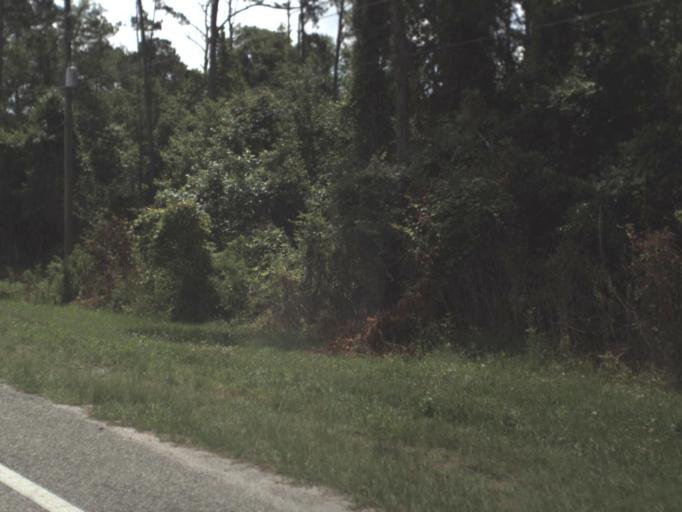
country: US
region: Florida
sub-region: Putnam County
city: East Palatka
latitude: 29.7255
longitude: -81.4793
